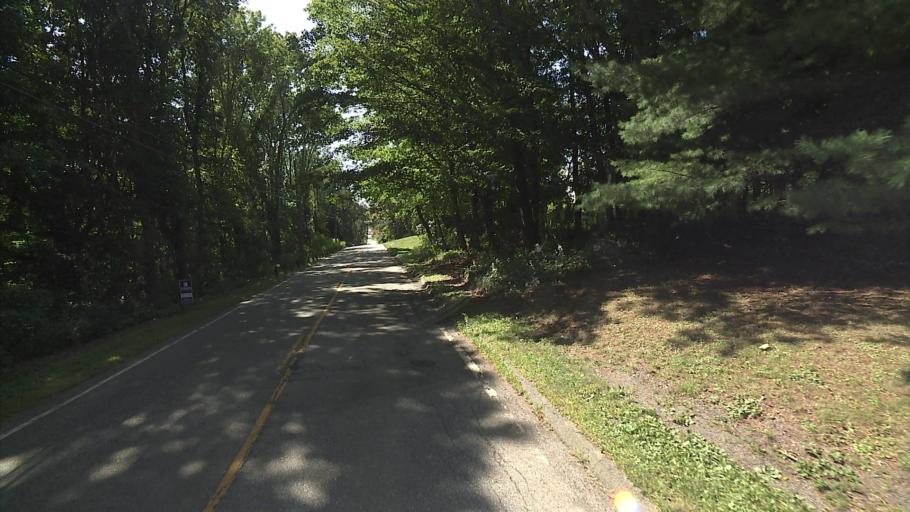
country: US
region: Connecticut
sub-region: Litchfield County
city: Northwest Harwinton
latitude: 41.7444
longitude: -73.0789
